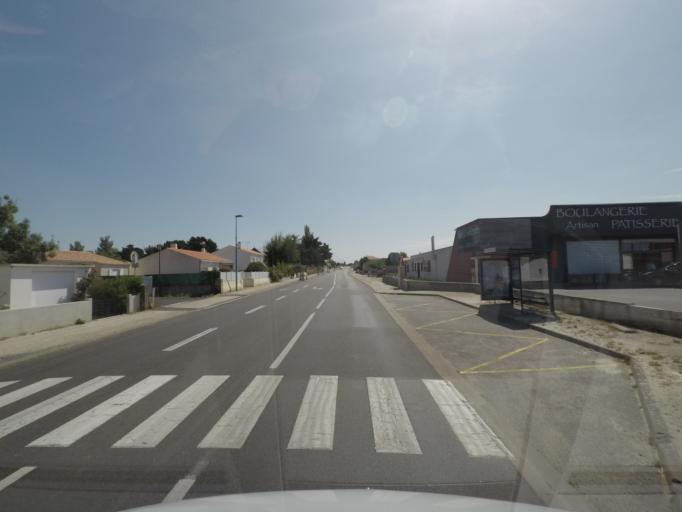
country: FR
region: Pays de la Loire
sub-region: Departement de la Vendee
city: Beauvoir-sur-Mer
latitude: 46.9121
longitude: -2.0374
